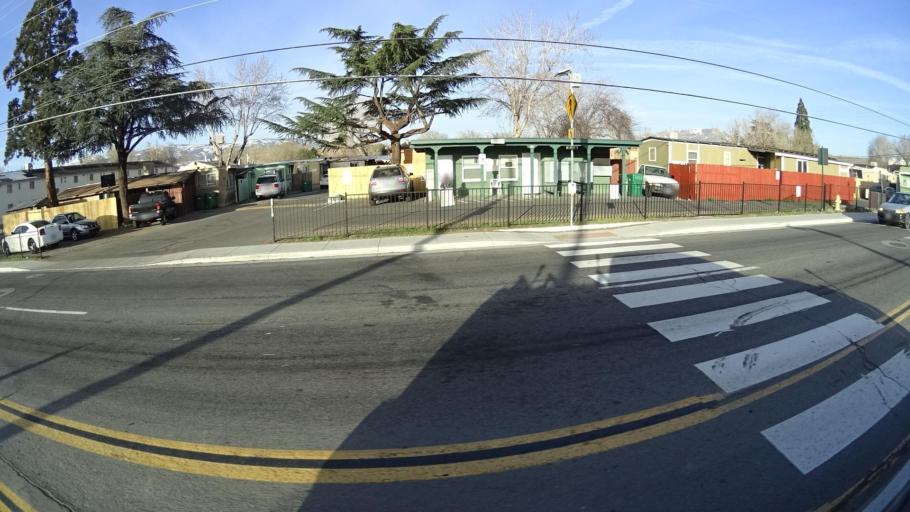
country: US
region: Nevada
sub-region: Washoe County
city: Sparks
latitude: 39.5377
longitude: -119.7755
